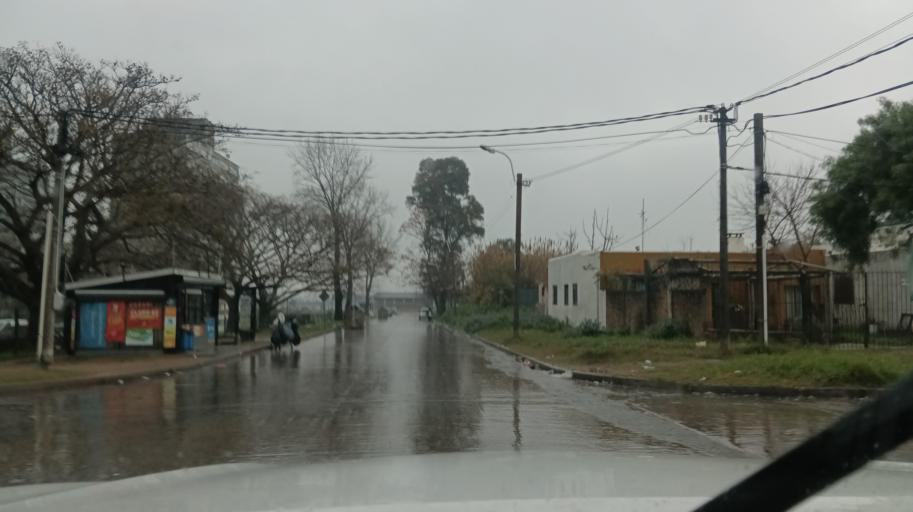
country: UY
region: Canelones
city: Paso de Carrasco
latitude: -34.8745
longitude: -56.1224
